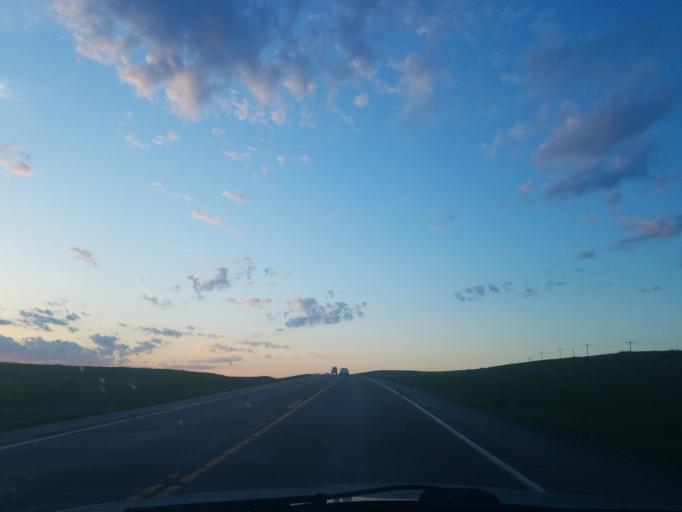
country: US
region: North Dakota
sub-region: McKenzie County
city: Watford City
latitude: 47.6492
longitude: -103.2701
